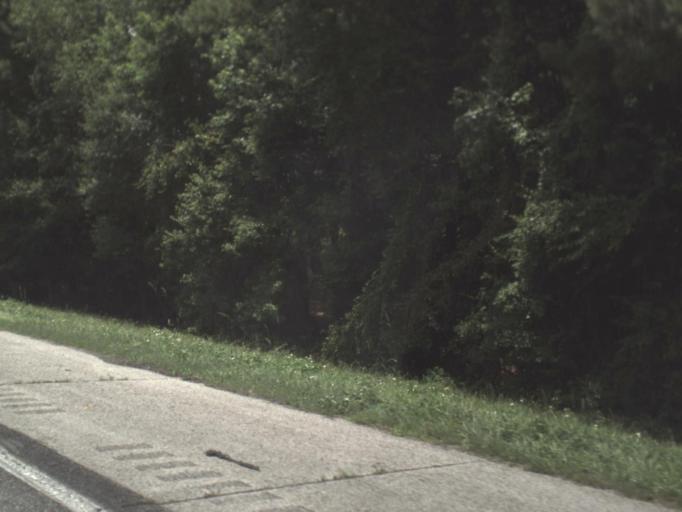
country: US
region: Florida
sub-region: Alachua County
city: High Springs
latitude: 29.9239
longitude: -82.5577
